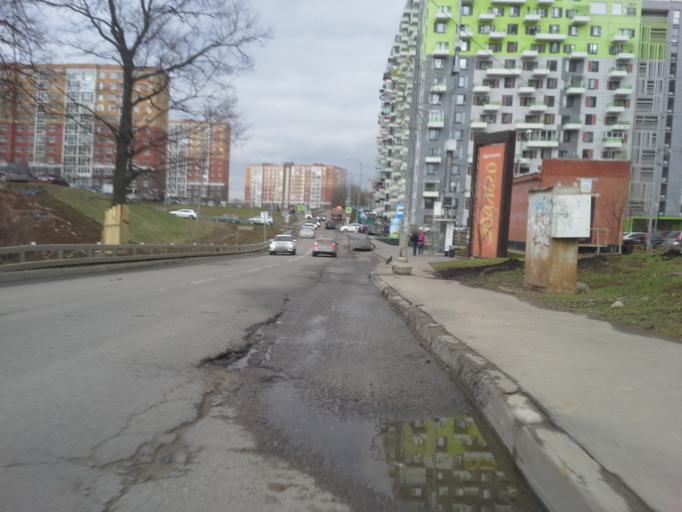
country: RU
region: Moskovskaya
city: Kommunarka
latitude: 55.5742
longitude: 37.4846
